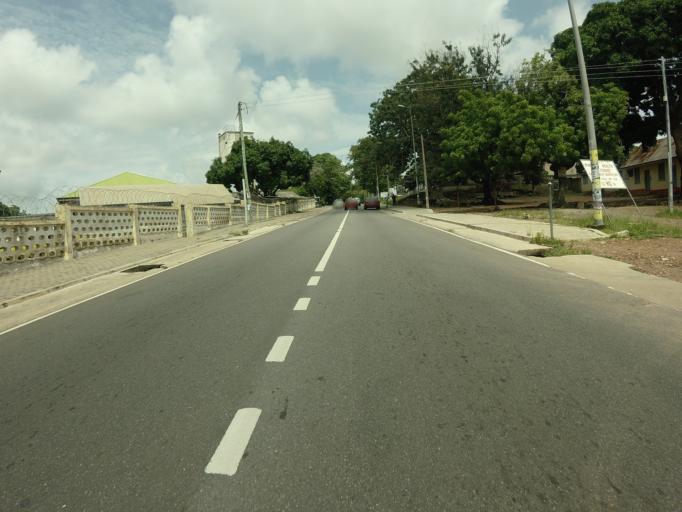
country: GH
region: Volta
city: Ho
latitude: 6.6103
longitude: 0.4680
